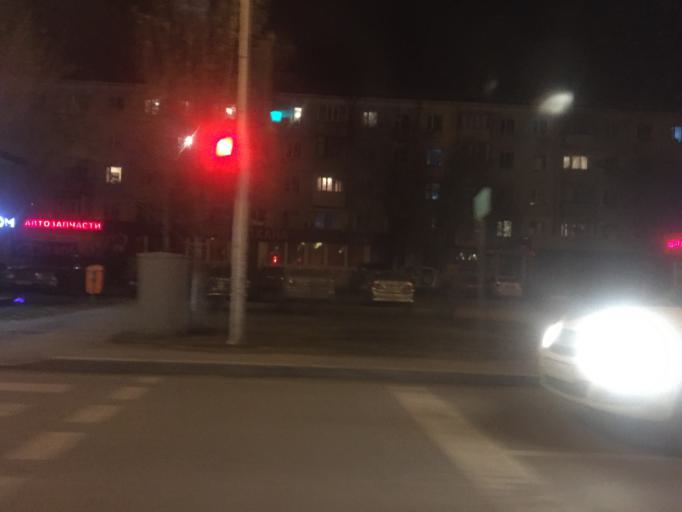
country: KZ
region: Astana Qalasy
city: Astana
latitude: 51.1834
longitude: 71.4088
